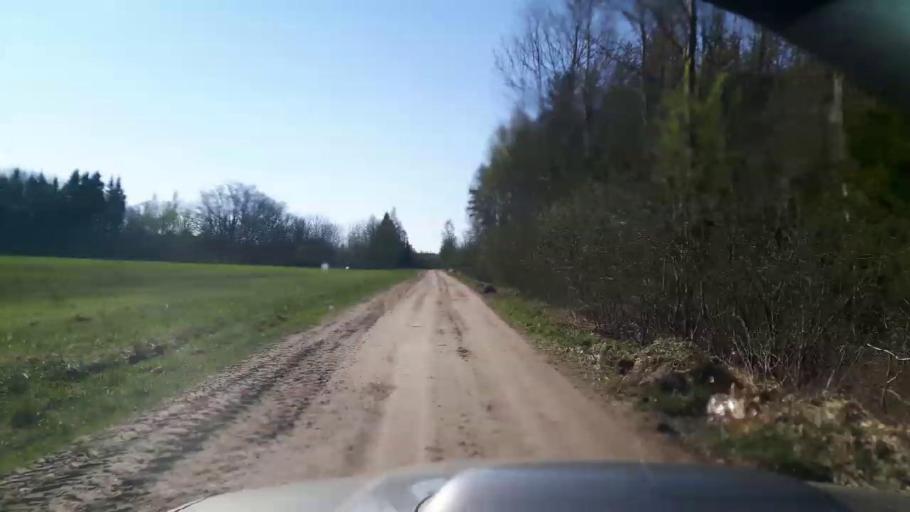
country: EE
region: Paernumaa
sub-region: Tootsi vald
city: Tootsi
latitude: 58.5056
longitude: 24.9384
